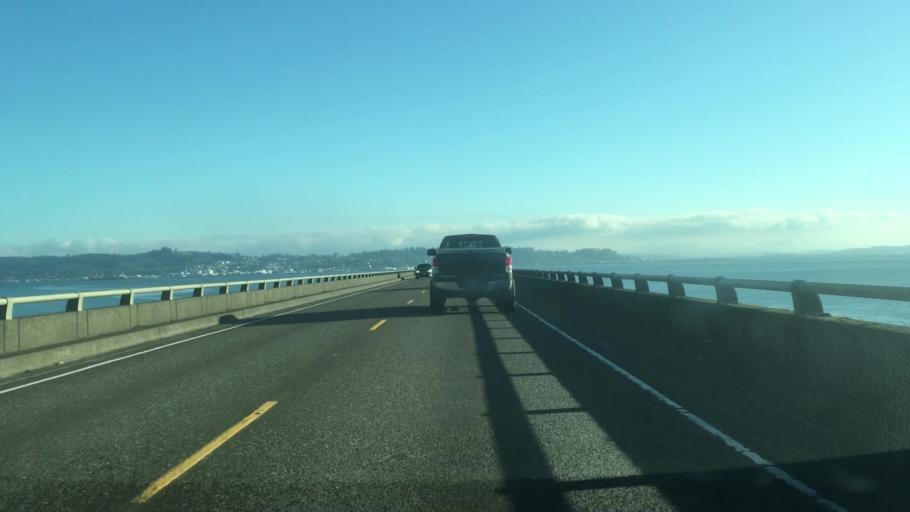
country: US
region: Oregon
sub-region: Clatsop County
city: Astoria
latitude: 46.2296
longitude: -123.8692
